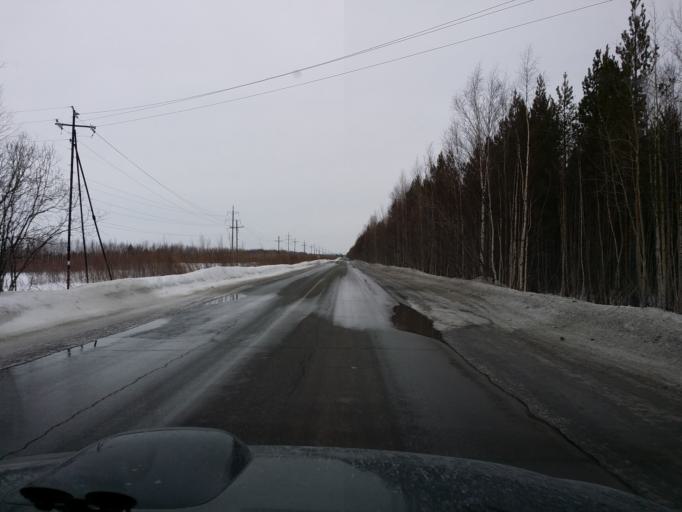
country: RU
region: Tomsk
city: Strezhevoy
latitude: 60.8014
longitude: 77.2939
